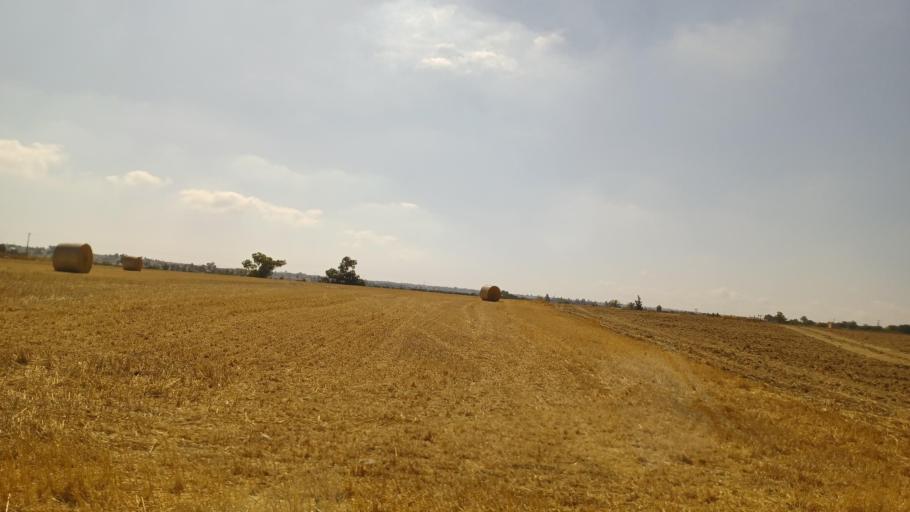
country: CY
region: Ammochostos
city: Acheritou
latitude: 35.0696
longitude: 33.8656
